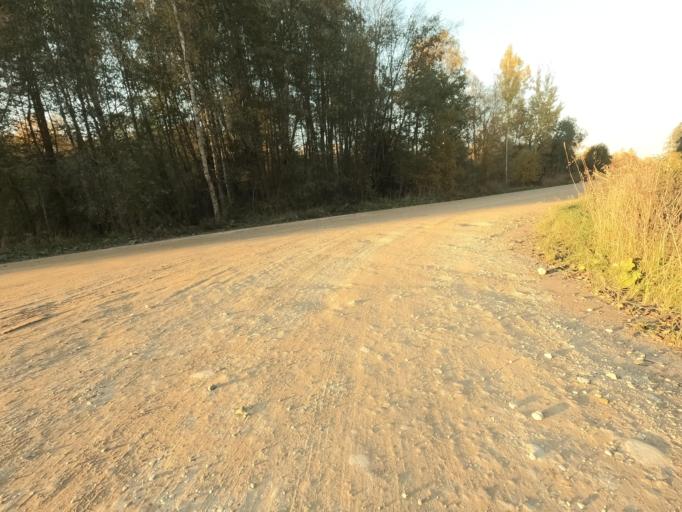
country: RU
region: Leningrad
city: Lyuban'
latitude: 59.0159
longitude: 31.0839
